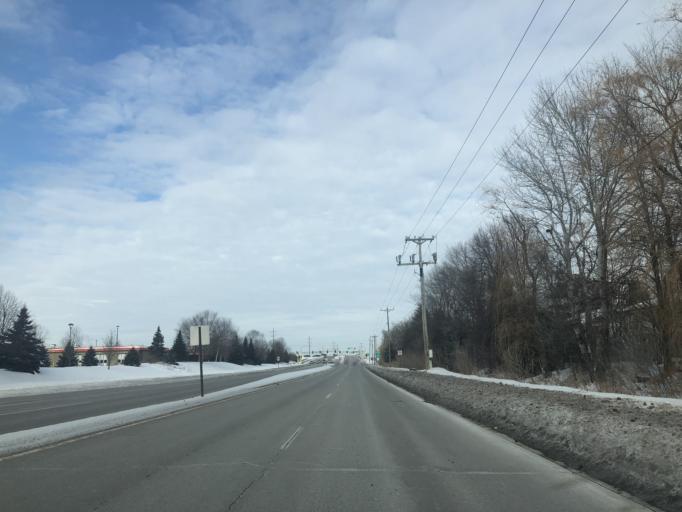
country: US
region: Minnesota
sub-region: Anoka County
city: Lexington
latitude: 45.1539
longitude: -93.1633
